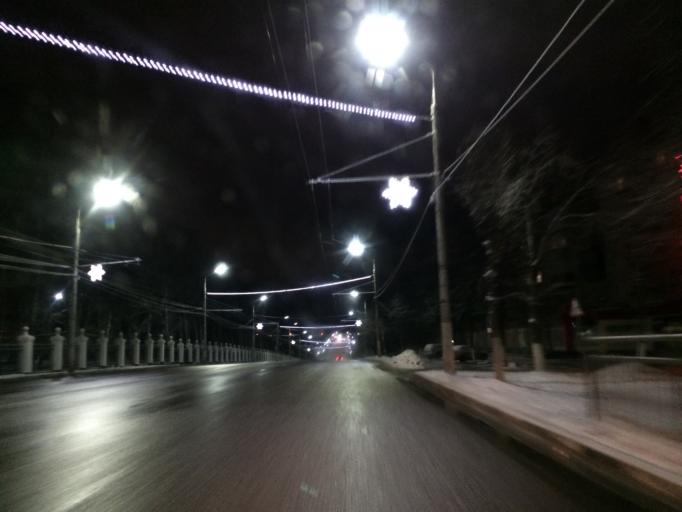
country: RU
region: Tula
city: Gorelki
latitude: 54.2281
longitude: 37.6284
